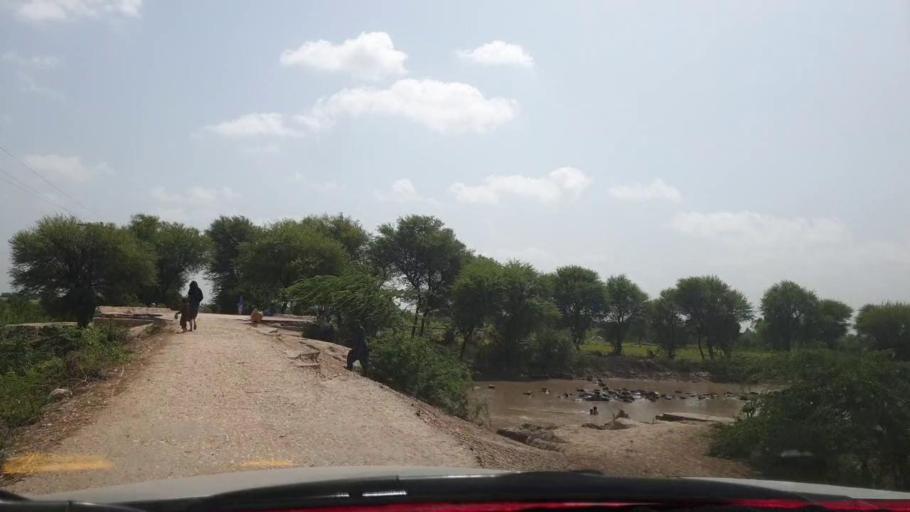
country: PK
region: Sindh
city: Talhar
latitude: 24.9010
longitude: 68.9056
